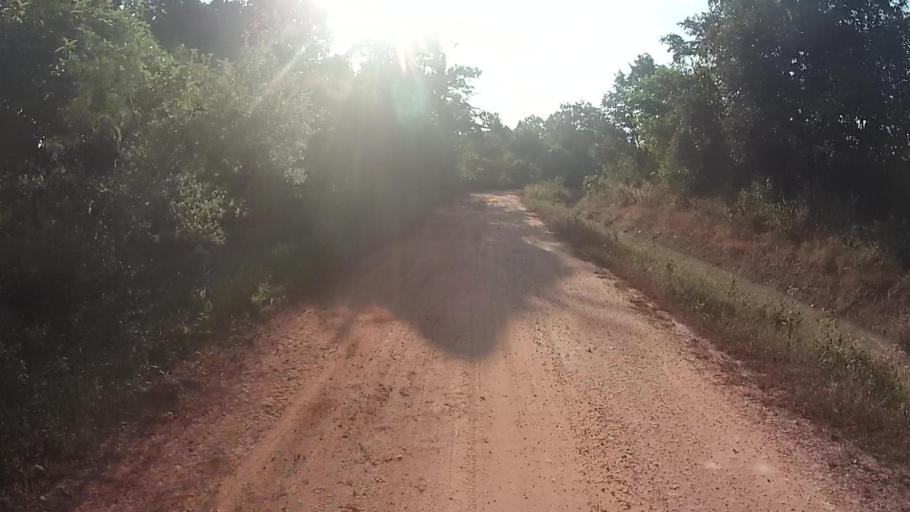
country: TH
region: Chiang Mai
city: San Sai
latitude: 18.9139
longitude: 99.0709
